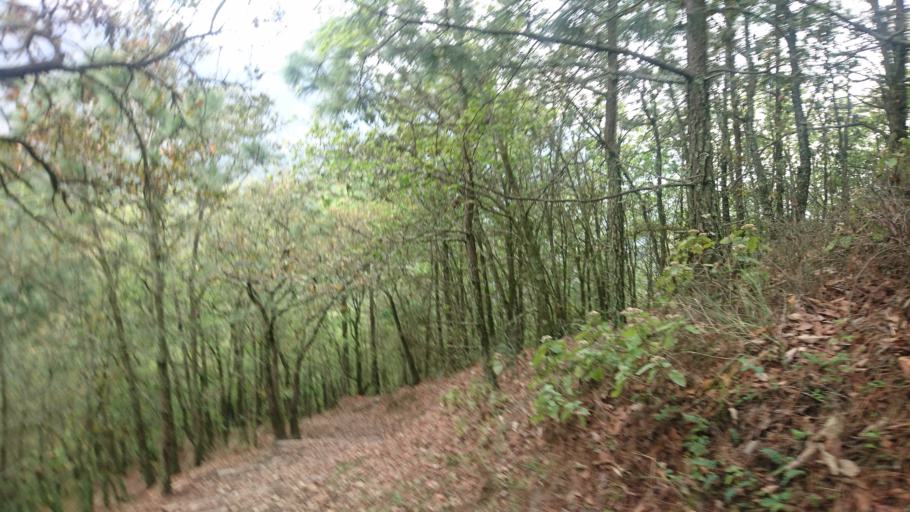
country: MX
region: Nuevo Leon
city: Garza Garcia
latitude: 25.6015
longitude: -100.3329
